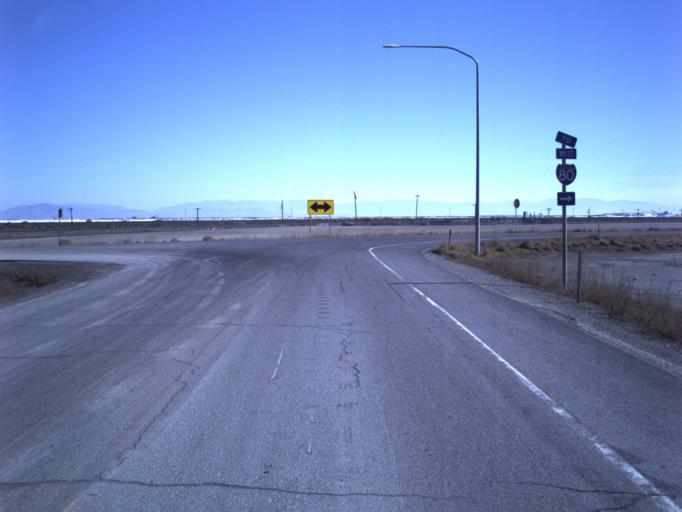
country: US
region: Utah
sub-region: Tooele County
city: Grantsville
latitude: 40.7108
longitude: -112.5276
